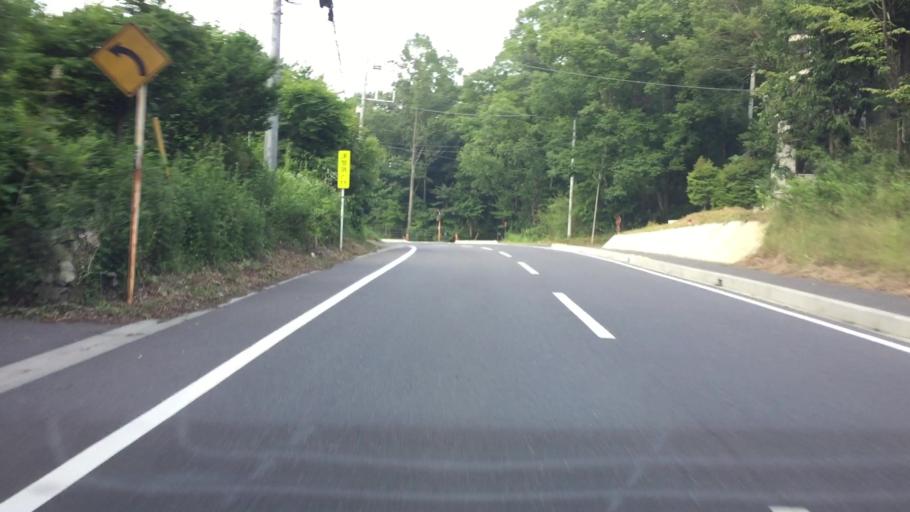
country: JP
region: Tochigi
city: Kuroiso
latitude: 37.0636
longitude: 140.0423
